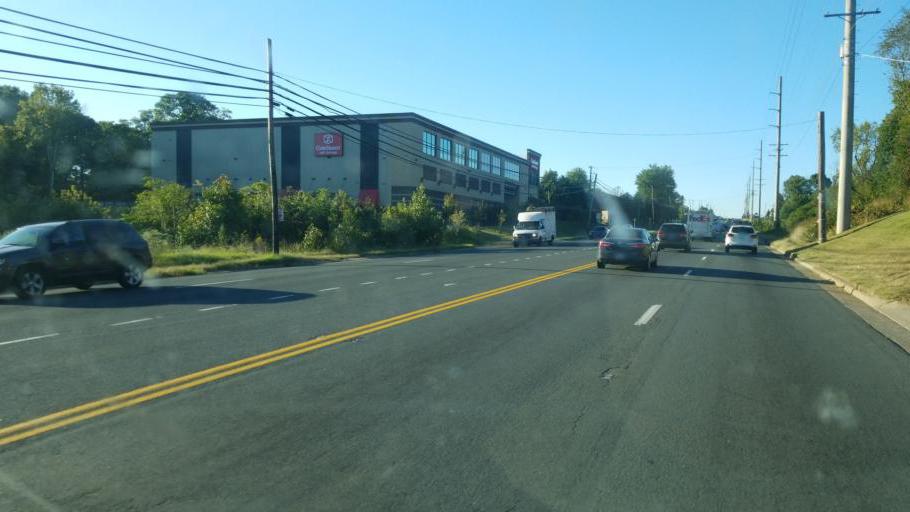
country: US
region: Virginia
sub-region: Prince William County
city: Yorkshire
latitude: 38.7864
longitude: -77.4492
